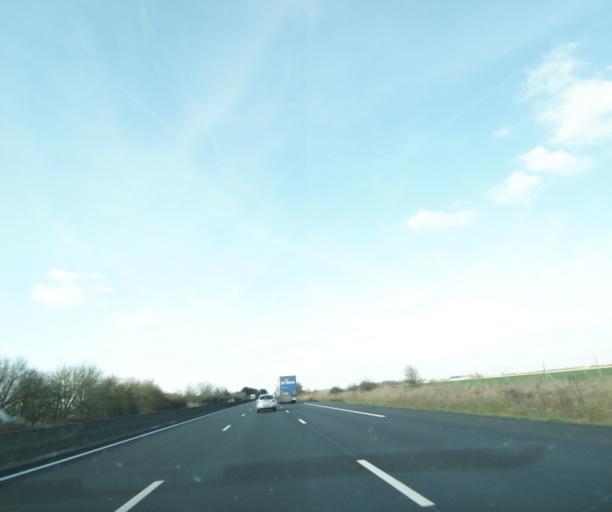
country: FR
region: Centre
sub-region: Departement d'Eure-et-Loir
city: Janville
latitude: 48.2166
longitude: 1.8470
